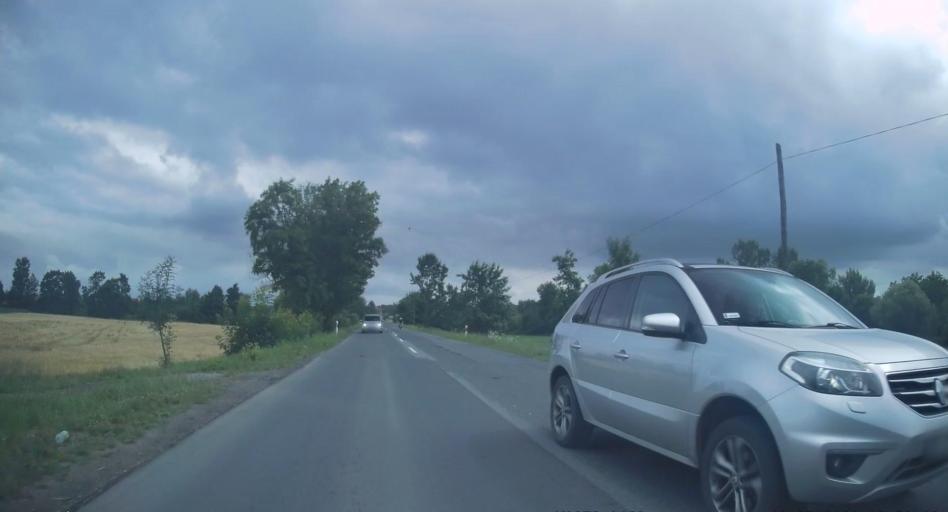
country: PL
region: Opole Voivodeship
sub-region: Powiat nyski
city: Paczkow
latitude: 50.4730
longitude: 17.0101
